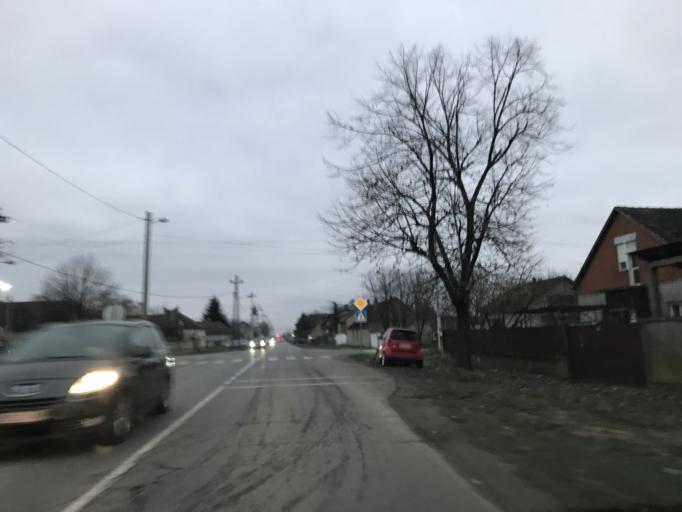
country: RS
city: Rumenka
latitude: 45.2942
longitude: 19.7372
